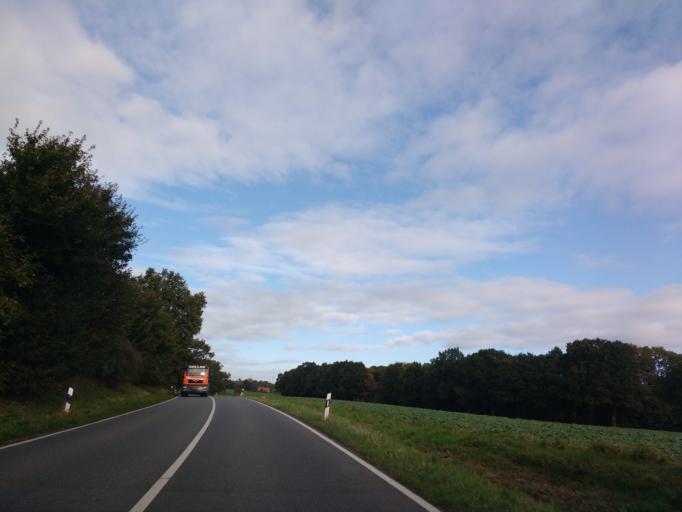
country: DE
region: Schleswig-Holstein
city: Altenkrempe
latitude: 54.1485
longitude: 10.8198
